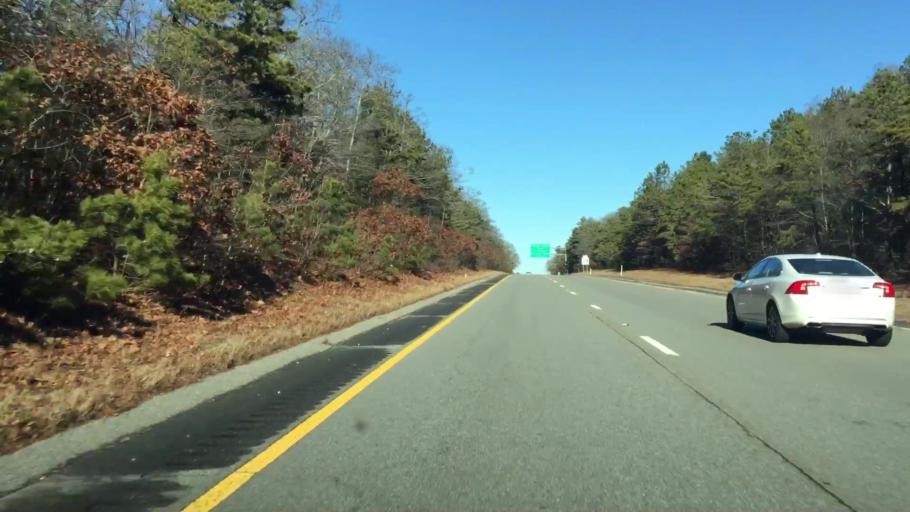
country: US
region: Massachusetts
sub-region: Barnstable County
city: West Falmouth
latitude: 41.5981
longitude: -70.6273
